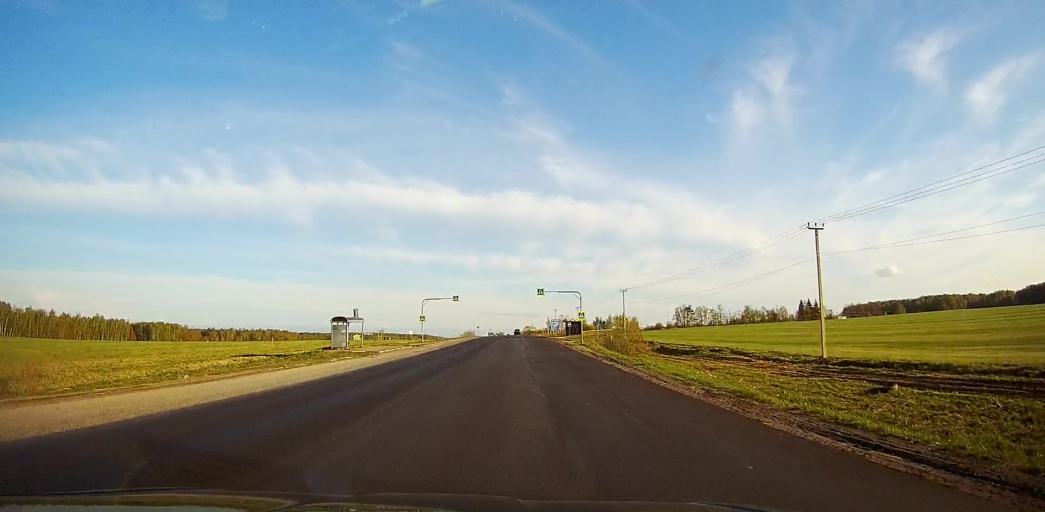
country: RU
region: Moskovskaya
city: Bronnitsy
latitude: 55.2979
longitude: 38.2114
